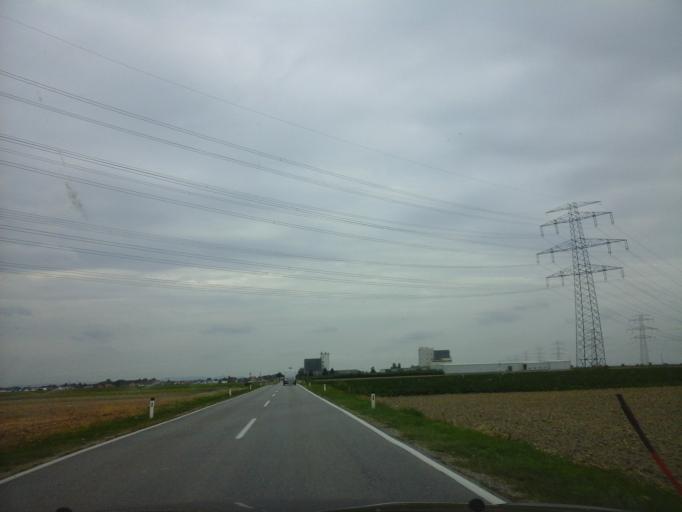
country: AT
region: Lower Austria
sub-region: Politischer Bezirk Ganserndorf
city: Mannsdorf an der Donau
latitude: 48.1624
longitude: 16.6377
